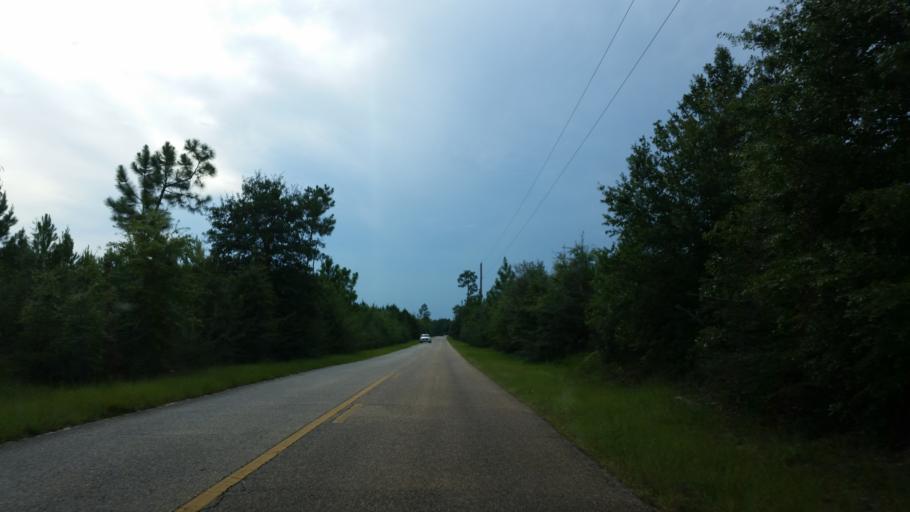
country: US
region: Florida
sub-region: Santa Rosa County
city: Point Baker
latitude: 30.7169
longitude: -86.9579
